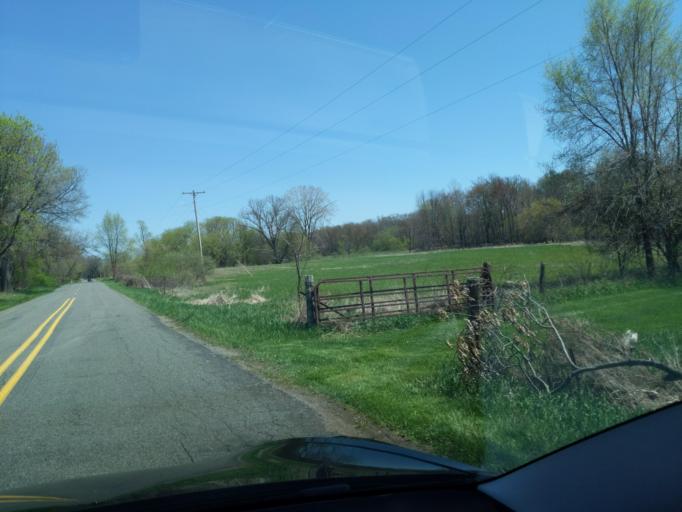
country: US
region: Michigan
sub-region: Ingham County
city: Stockbridge
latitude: 42.4921
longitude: -84.2168
